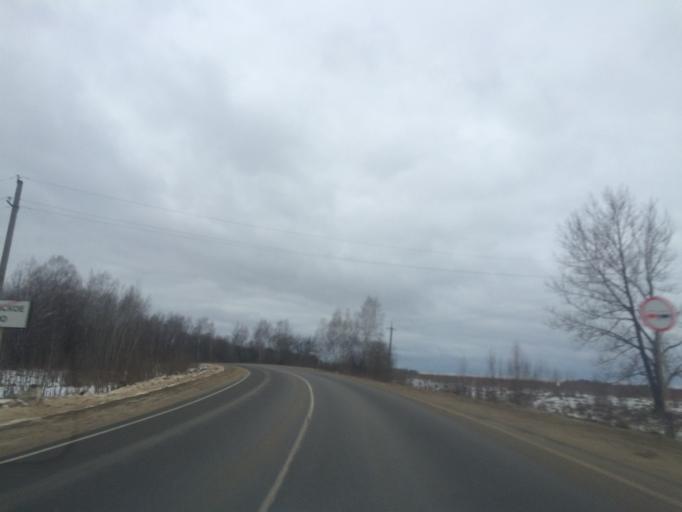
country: RU
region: Tula
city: Odoyev
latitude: 54.0082
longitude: 36.7742
